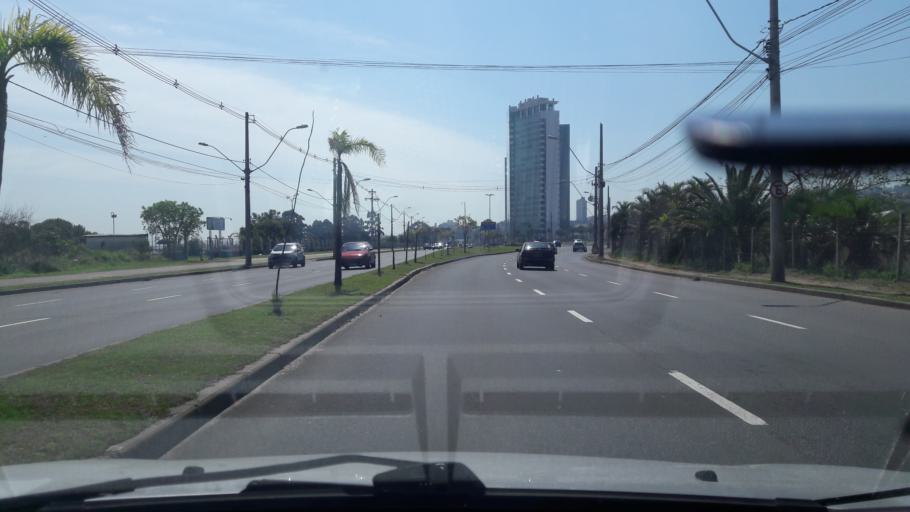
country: BR
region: Rio Grande do Sul
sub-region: Porto Alegre
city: Porto Alegre
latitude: -30.0904
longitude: -51.2487
